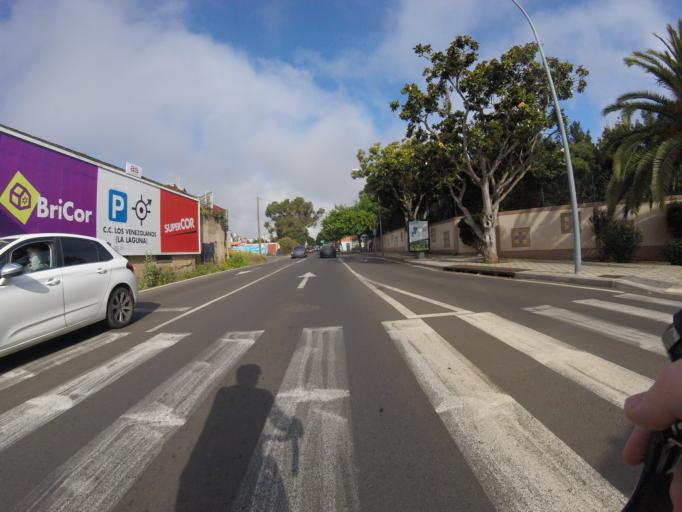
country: ES
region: Canary Islands
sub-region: Provincia de Santa Cruz de Tenerife
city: La Laguna
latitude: 28.4901
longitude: -16.3284
